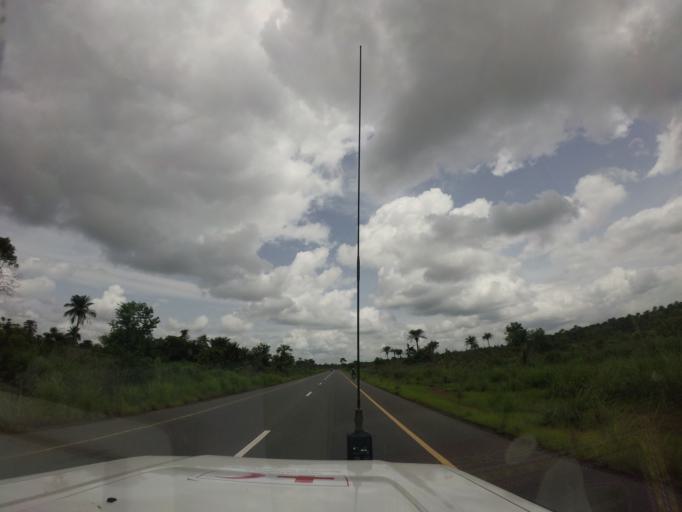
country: SL
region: Northern Province
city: Mange
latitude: 8.9460
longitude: -12.8636
